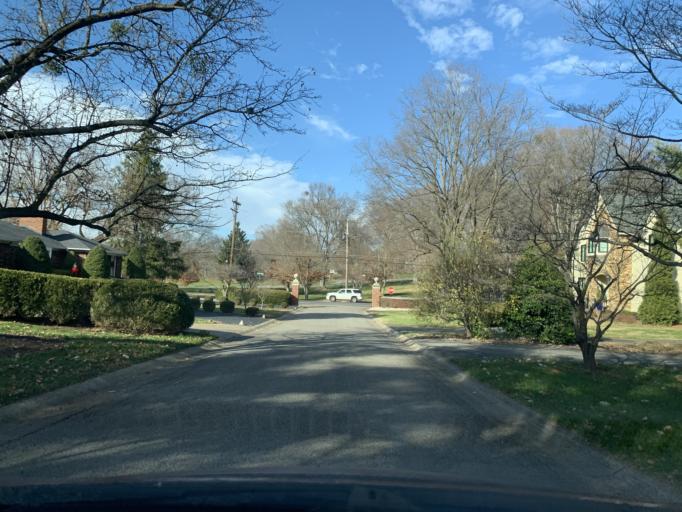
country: US
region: Kentucky
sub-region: Jefferson County
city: Saint Matthews
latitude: 38.2457
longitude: -85.6856
